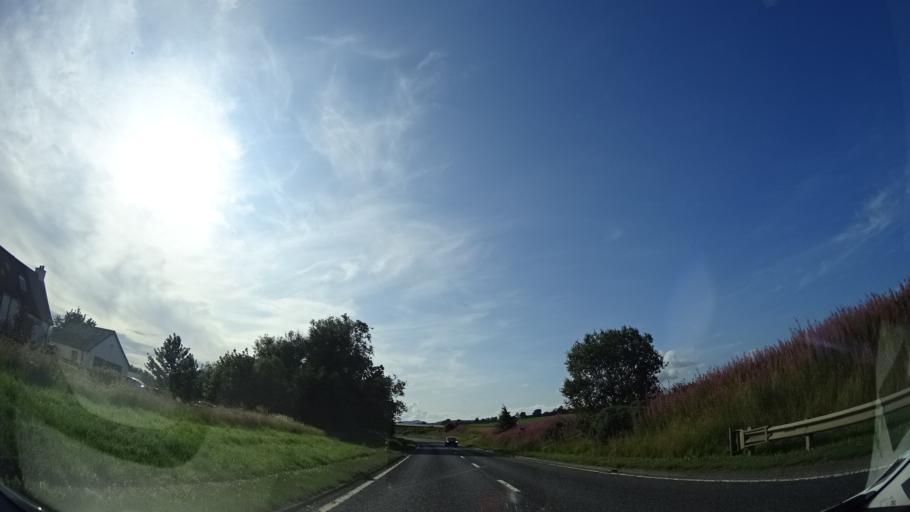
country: GB
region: Scotland
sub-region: Highland
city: Muir of Ord
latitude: 57.5601
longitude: -4.5519
